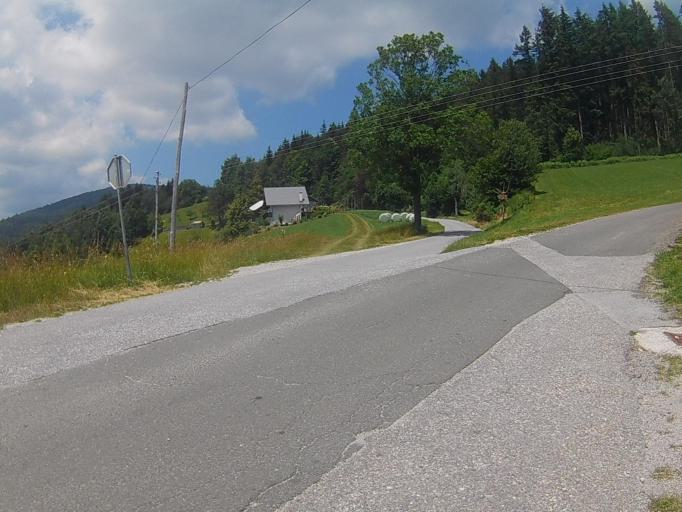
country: SI
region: Maribor
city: Pekre
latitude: 46.4947
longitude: 15.5674
